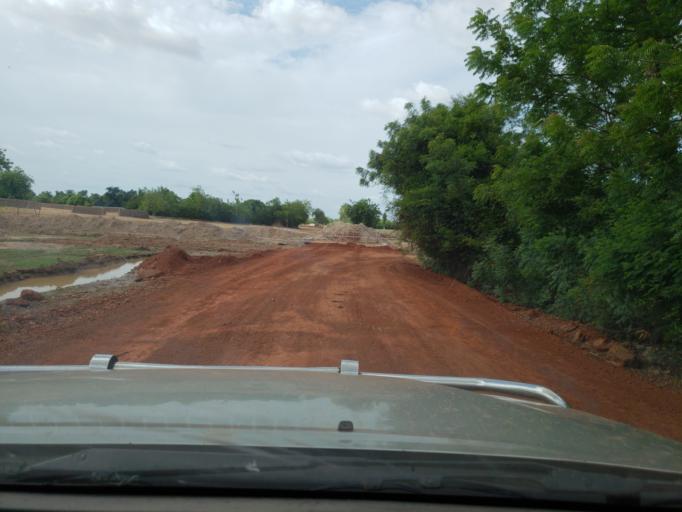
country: ML
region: Segou
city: Bla
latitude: 12.7275
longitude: -5.6731
